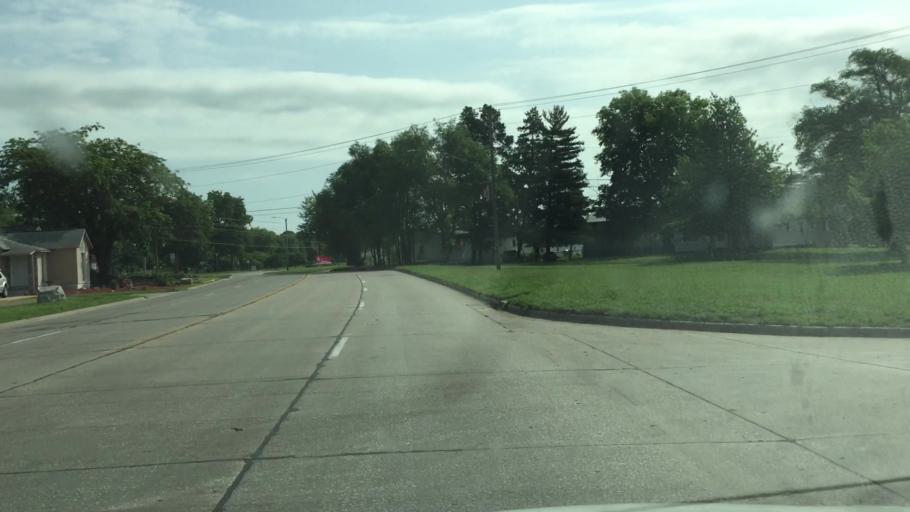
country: US
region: Iowa
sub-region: Lee County
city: Fort Madison
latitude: 40.6251
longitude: -91.3597
